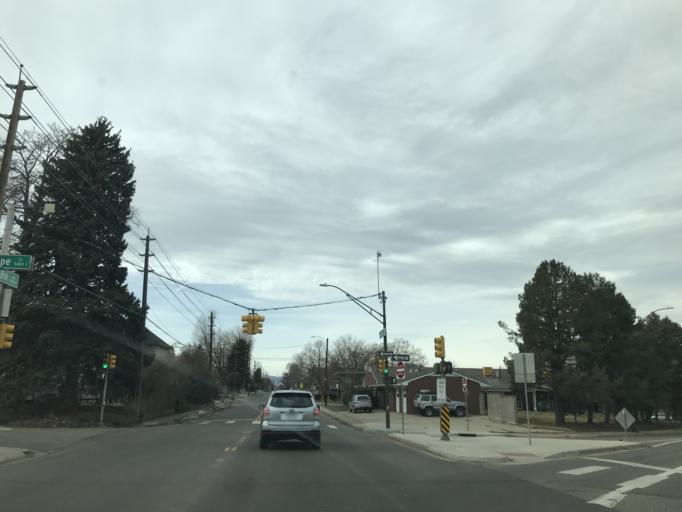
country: US
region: Colorado
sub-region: Arapahoe County
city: Glendale
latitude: 39.7293
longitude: -104.9247
